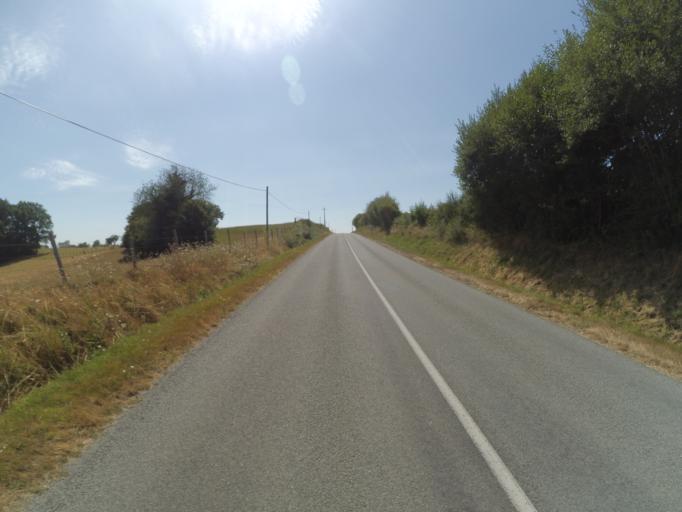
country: FR
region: Limousin
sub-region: Departement de la Creuse
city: Le Grand-Bourg
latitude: 46.1450
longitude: 1.6613
